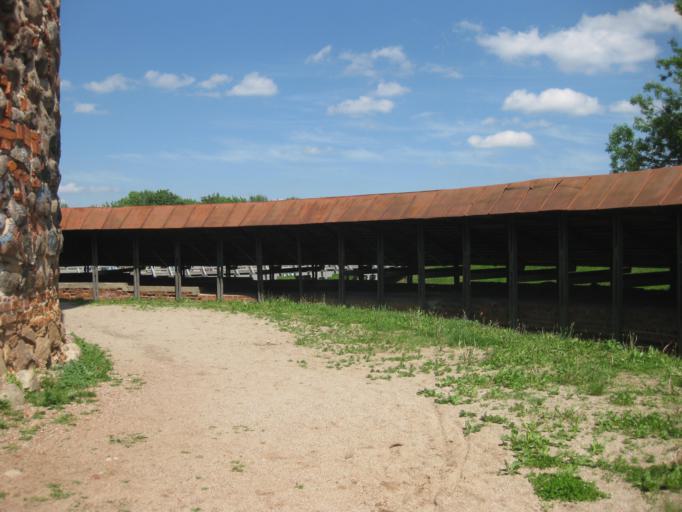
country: LT
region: Kauno apskritis
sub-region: Kaunas
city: Kaunas
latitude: 54.8987
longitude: 23.8854
